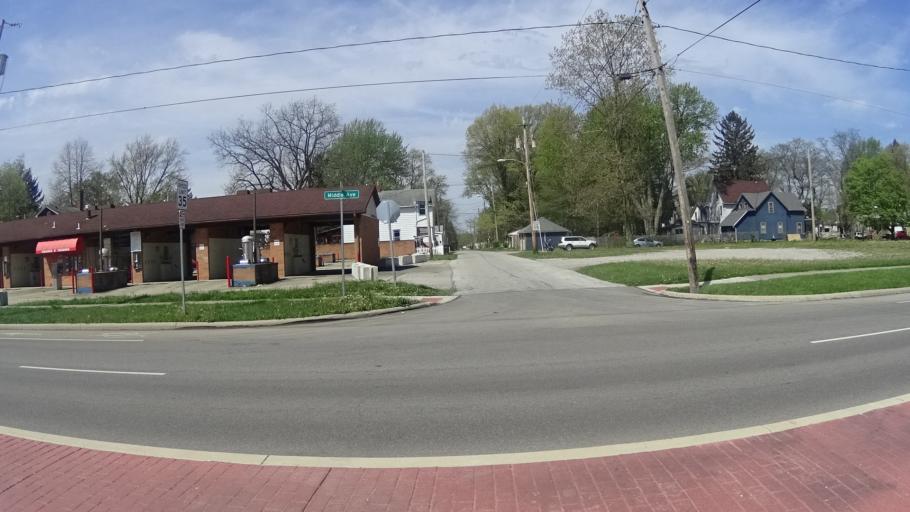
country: US
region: Ohio
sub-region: Lorain County
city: Elyria
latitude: 41.3591
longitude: -82.1072
